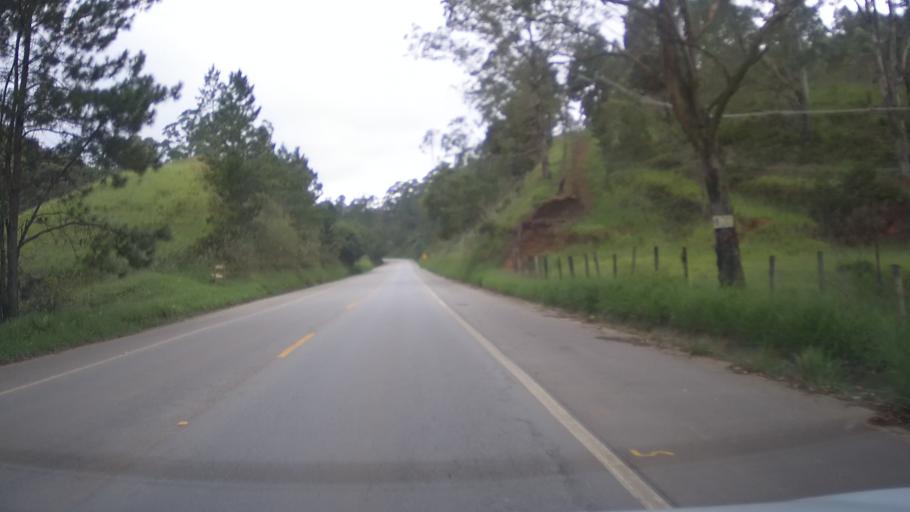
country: BR
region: Sao Paulo
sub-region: Aruja
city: Aruja
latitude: -23.3577
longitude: -46.4174
